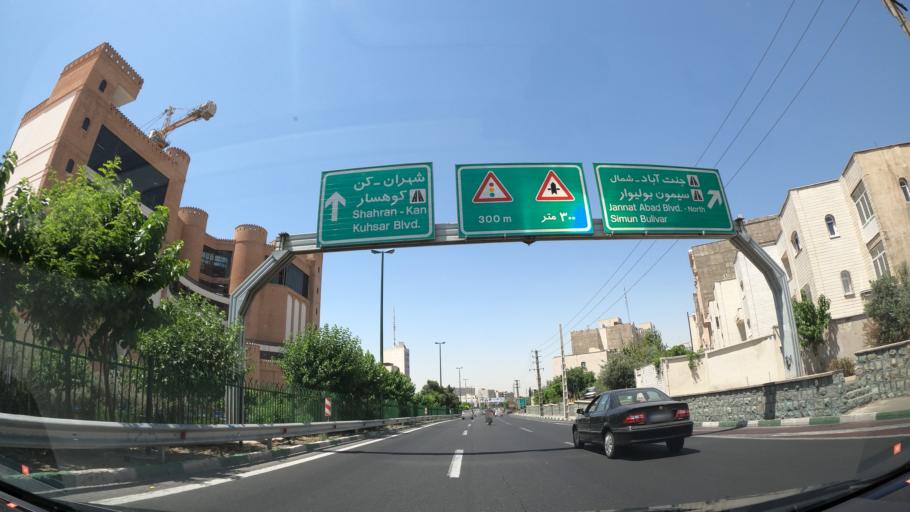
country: IR
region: Tehran
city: Tajrish
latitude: 35.7654
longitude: 51.3062
